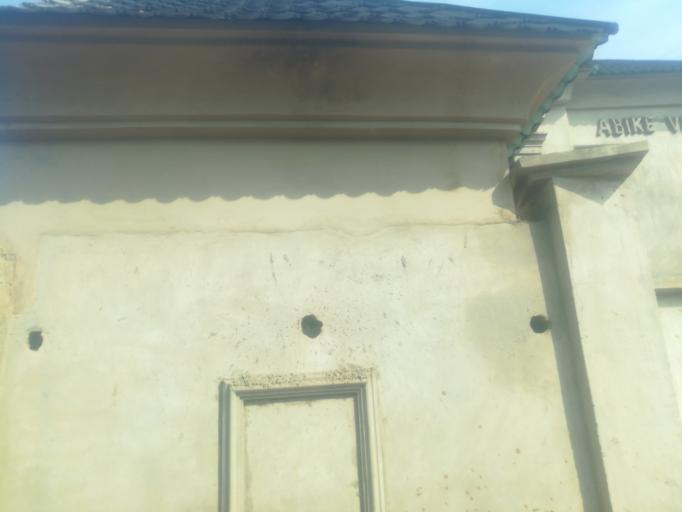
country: NG
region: Oyo
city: Ibadan
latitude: 7.3463
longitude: 3.8452
